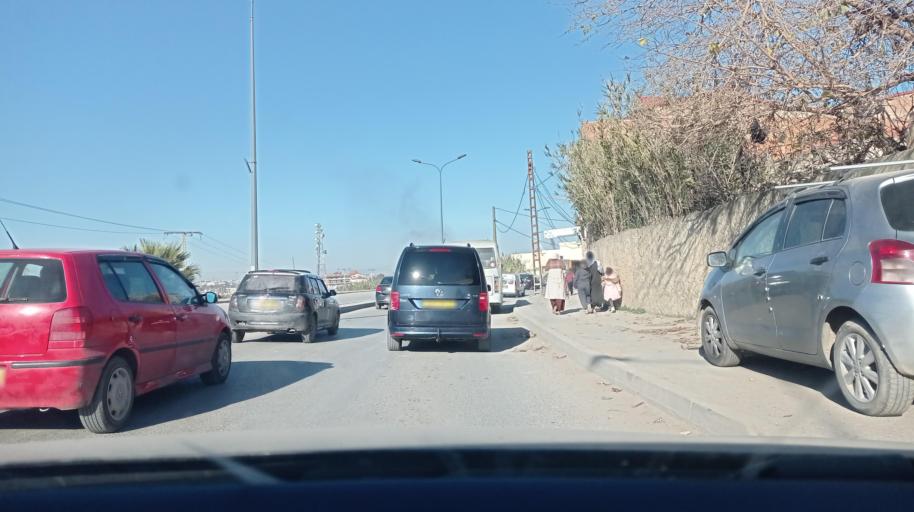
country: DZ
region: Tipaza
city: Baraki
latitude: 36.6696
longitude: 3.0858
